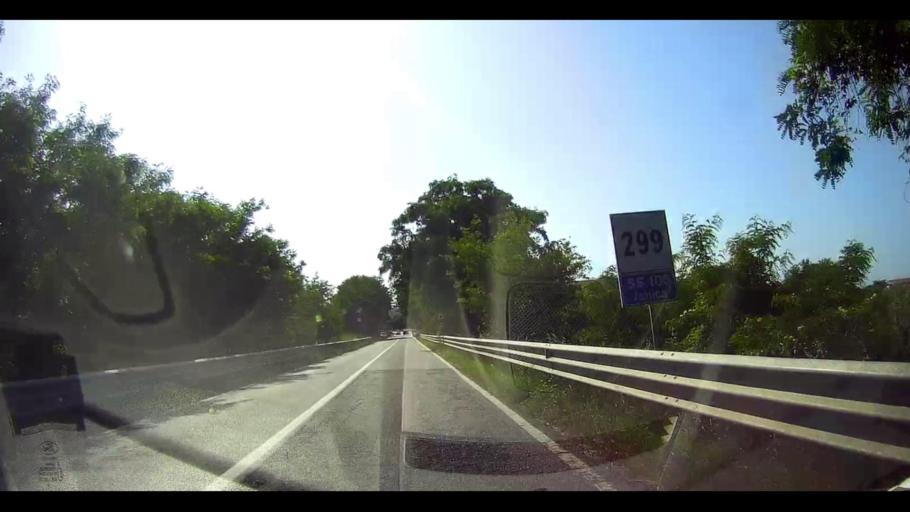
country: IT
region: Calabria
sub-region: Provincia di Cosenza
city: Cariati
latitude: 39.4833
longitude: 16.9762
